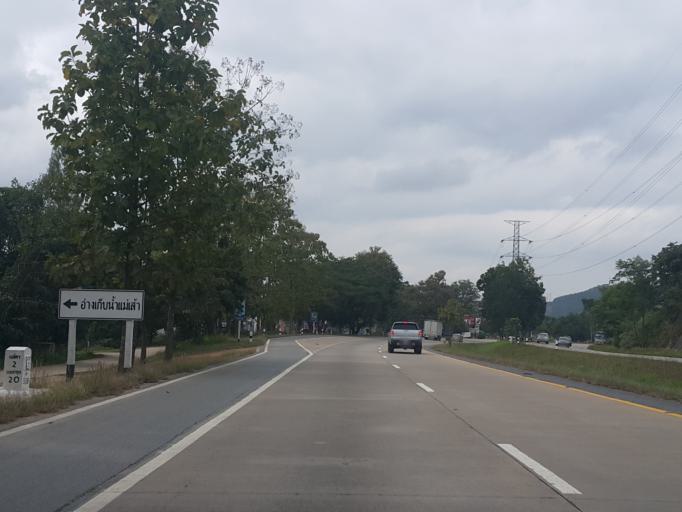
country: TH
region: Lamphun
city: Mae Tha
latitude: 18.4621
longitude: 99.1623
